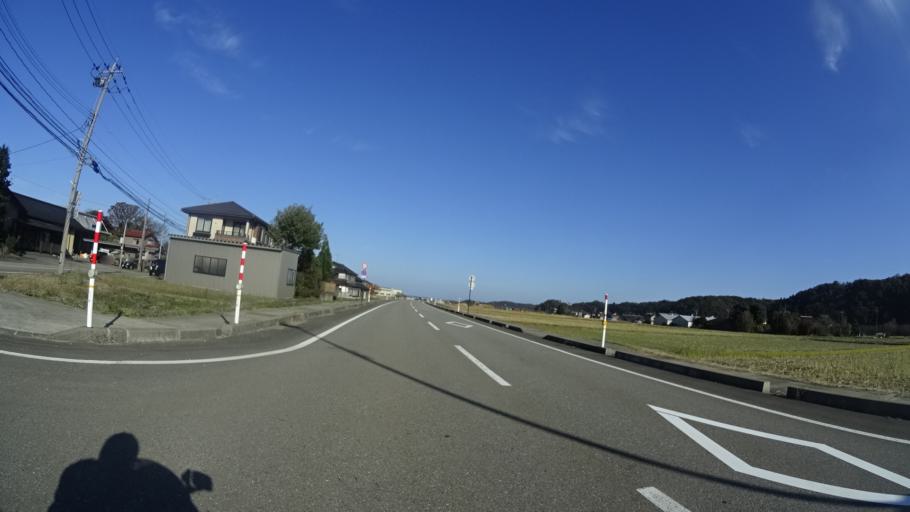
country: JP
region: Ishikawa
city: Komatsu
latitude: 36.2869
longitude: 136.3901
